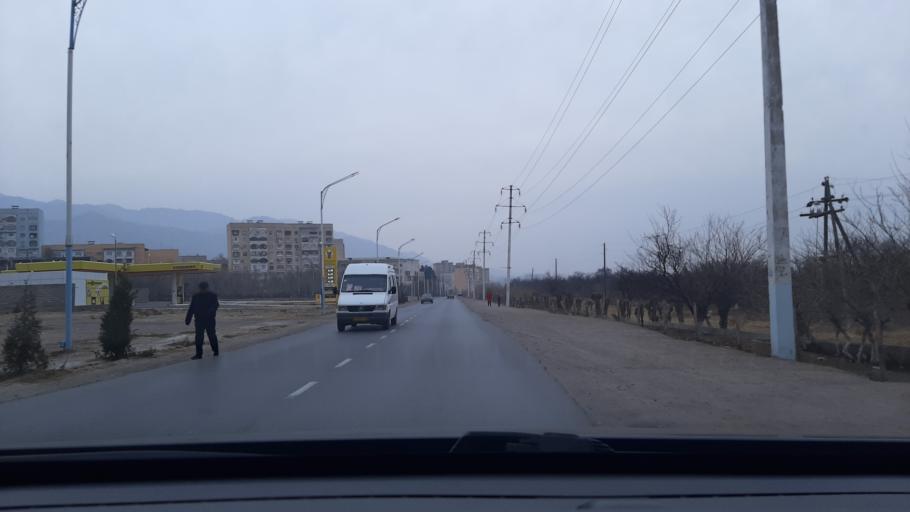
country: TJ
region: Viloyati Sughd
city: Khujand
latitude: 40.2834
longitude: 69.5879
